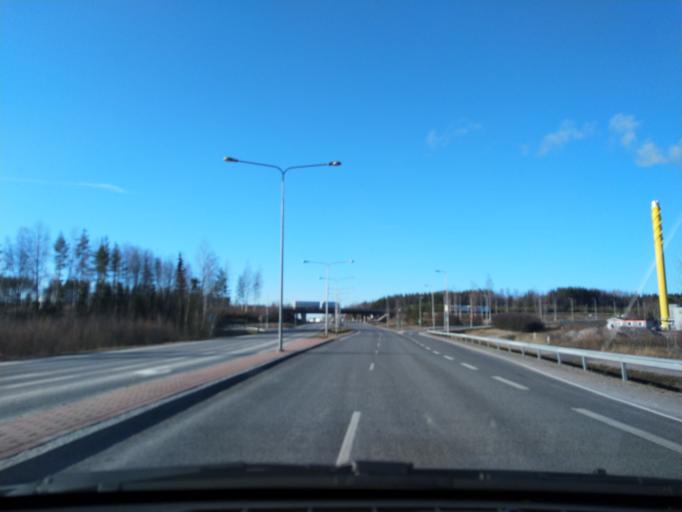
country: FI
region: Uusimaa
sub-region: Helsinki
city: Jaervenpaeae
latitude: 60.4530
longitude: 25.1307
